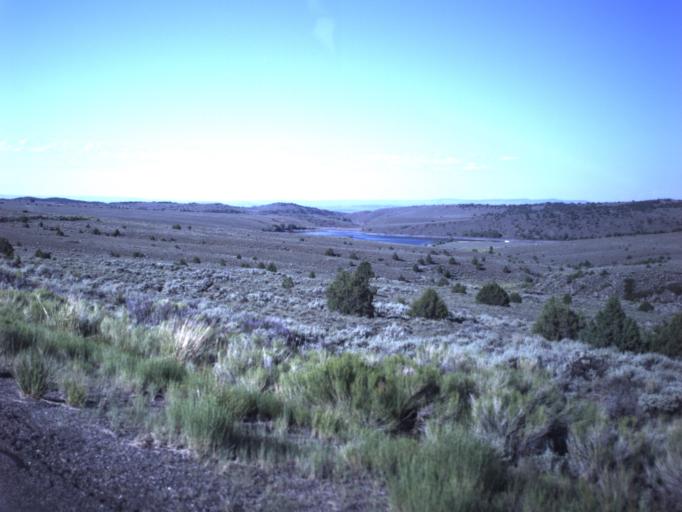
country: US
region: Utah
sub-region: Wayne County
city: Loa
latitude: 38.5328
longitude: -111.5144
